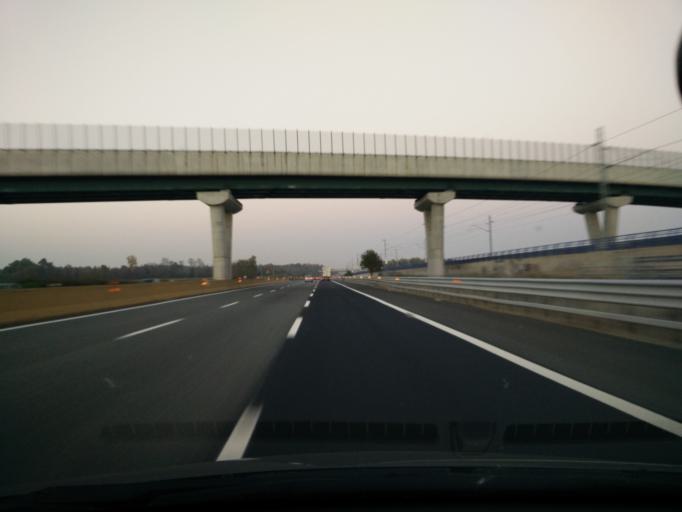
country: IT
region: Piedmont
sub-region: Provincia di Vercelli
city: Carisio
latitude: 45.4064
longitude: 8.1652
